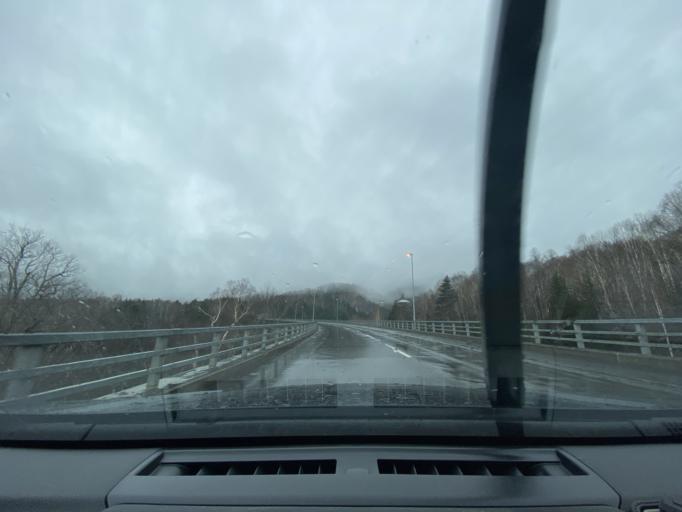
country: JP
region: Hokkaido
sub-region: Asahikawa-shi
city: Asahikawa
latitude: 43.8162
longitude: 142.2495
